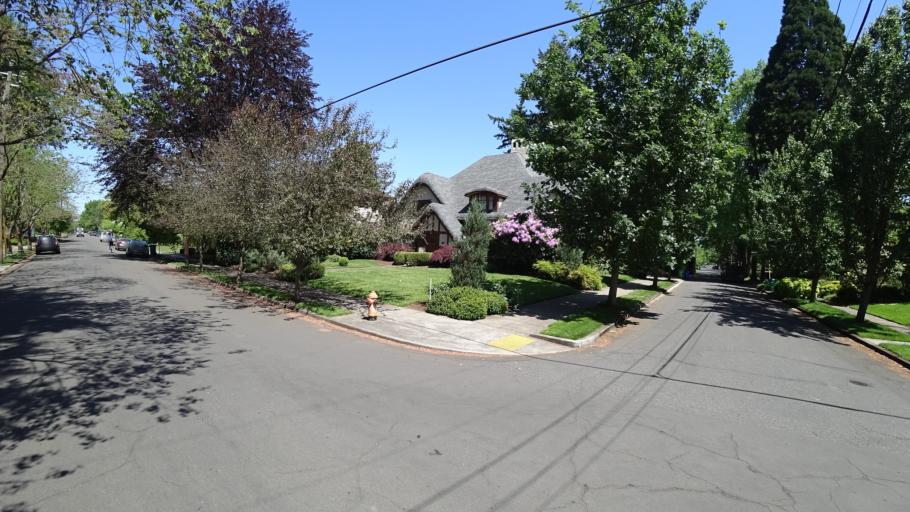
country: US
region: Oregon
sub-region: Multnomah County
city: Portland
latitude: 45.5379
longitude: -122.6368
